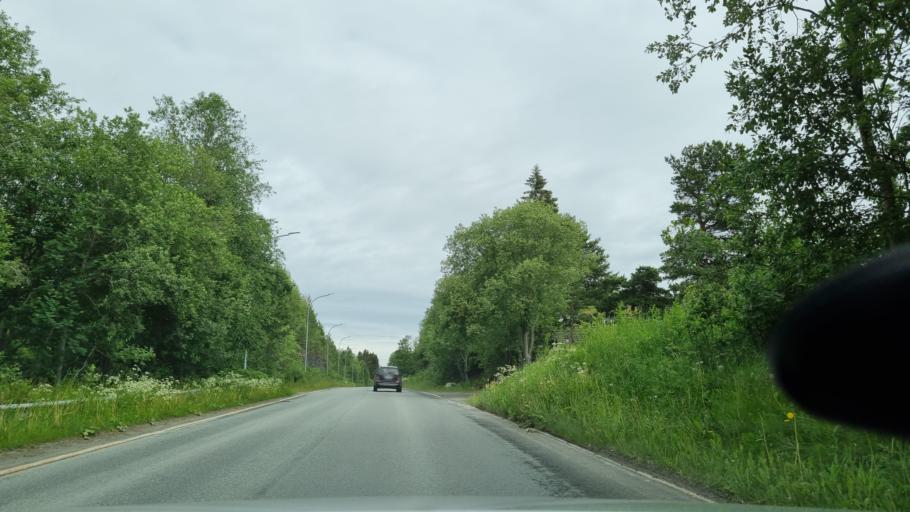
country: NO
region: Sor-Trondelag
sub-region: Melhus
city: Melhus
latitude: 63.3552
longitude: 10.3378
